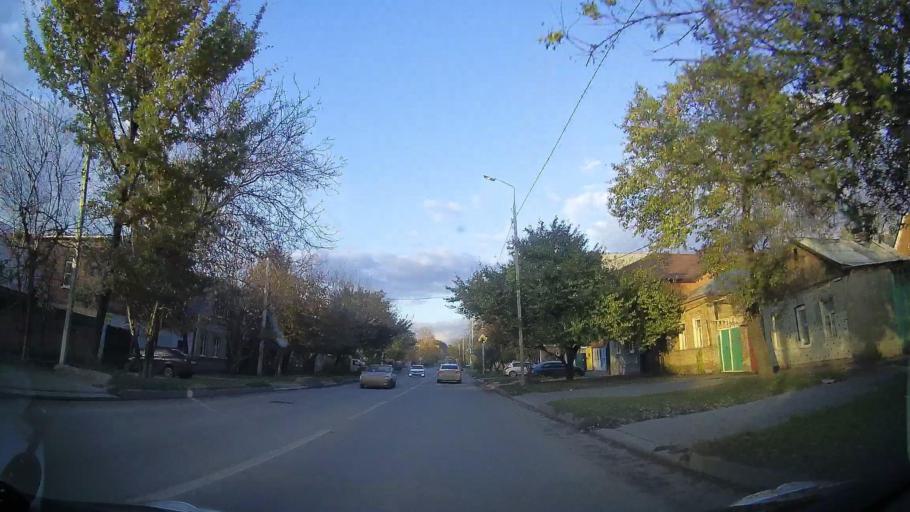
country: RU
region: Rostov
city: Imeni Chkalova
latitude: 47.2685
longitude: 39.7789
